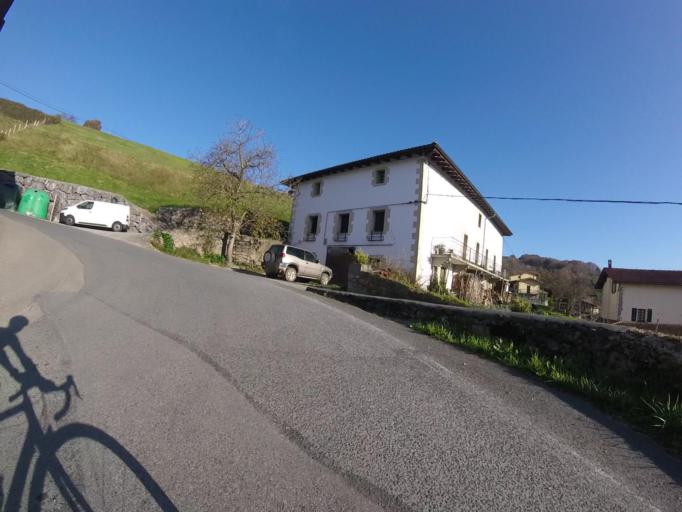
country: ES
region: Navarre
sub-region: Provincia de Navarra
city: Igantzi
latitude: 43.2261
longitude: -1.7016
